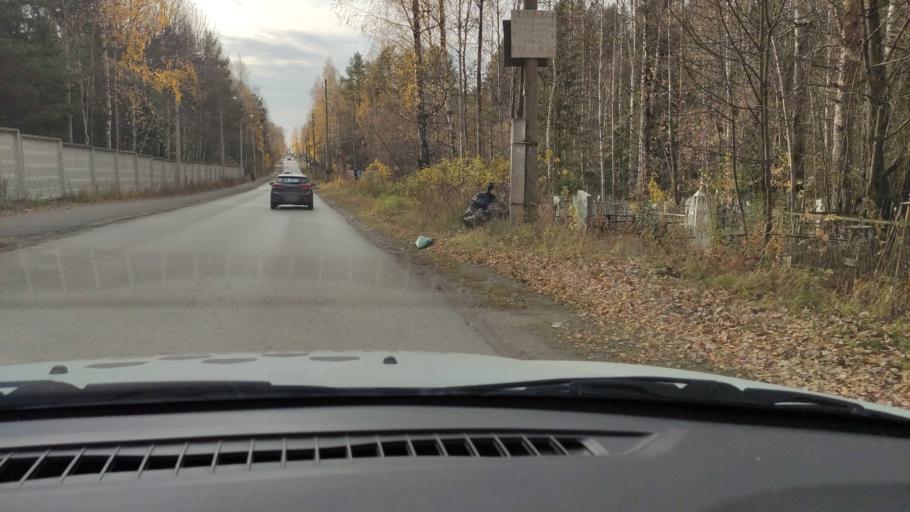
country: RU
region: Perm
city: Kondratovo
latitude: 58.0632
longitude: 56.1253
